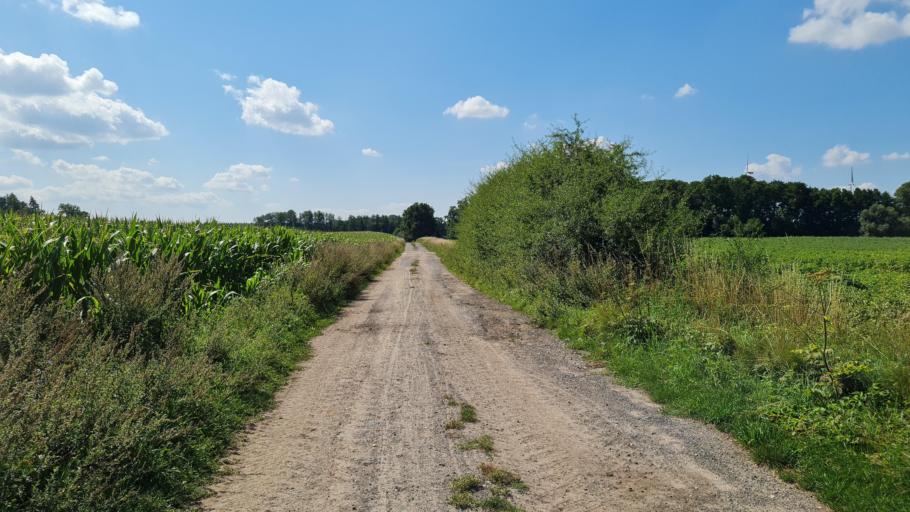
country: DE
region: Lower Saxony
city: Boitze
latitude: 53.1691
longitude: 10.7619
